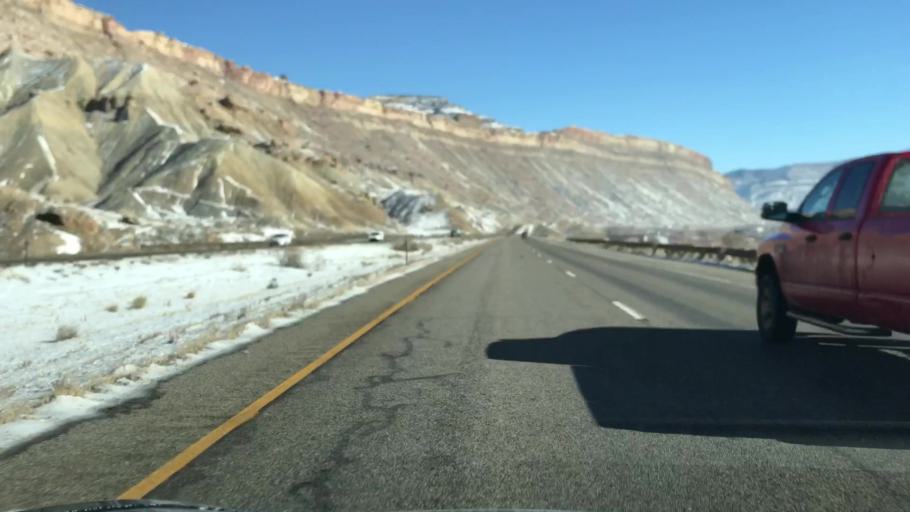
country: US
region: Colorado
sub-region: Mesa County
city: Palisade
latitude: 39.1168
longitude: -108.3927
